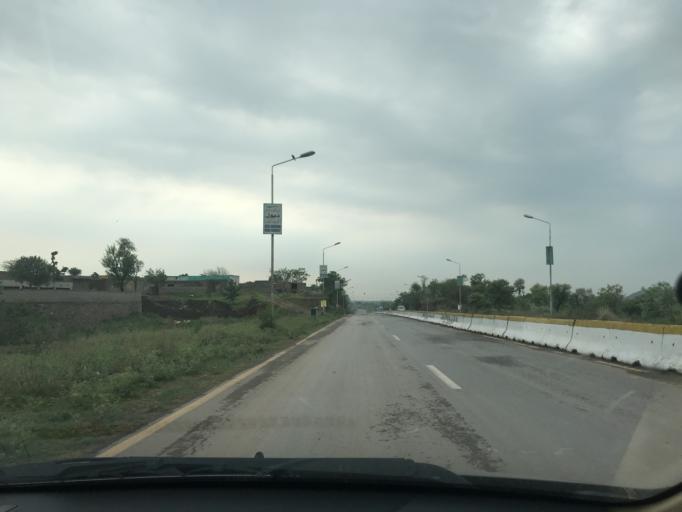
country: PK
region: Islamabad
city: Islamabad
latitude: 33.7008
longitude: 73.1865
